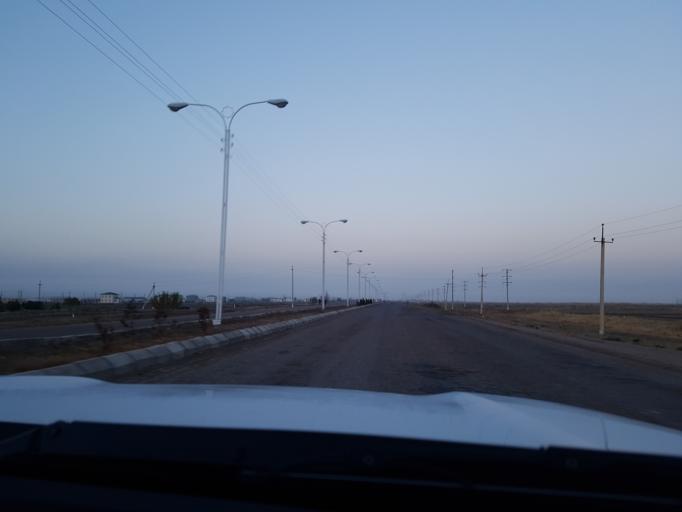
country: TM
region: Dasoguz
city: Koeneuergench
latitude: 41.7425
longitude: 58.7112
